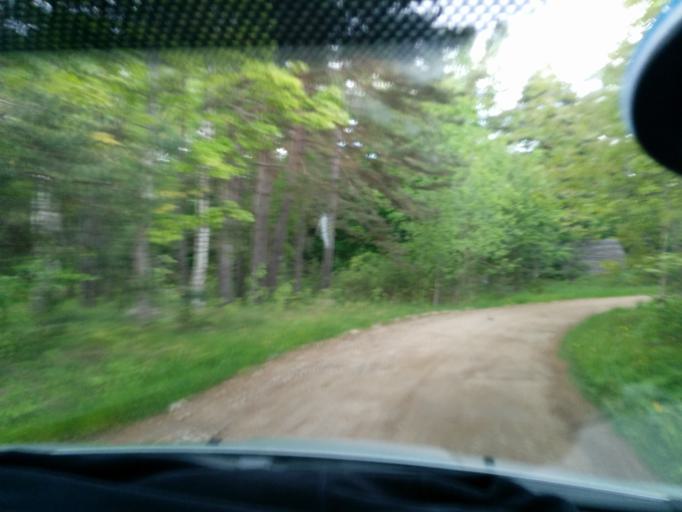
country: EE
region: Harju
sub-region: Loksa linn
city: Loksa
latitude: 59.6642
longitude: 25.7021
